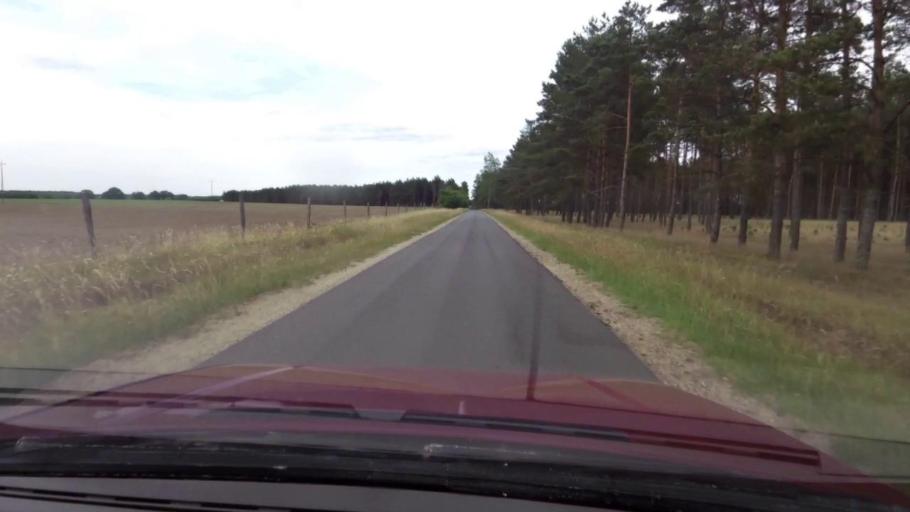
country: PL
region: Pomeranian Voivodeship
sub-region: Powiat bytowski
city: Trzebielino
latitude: 54.1963
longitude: 17.0688
